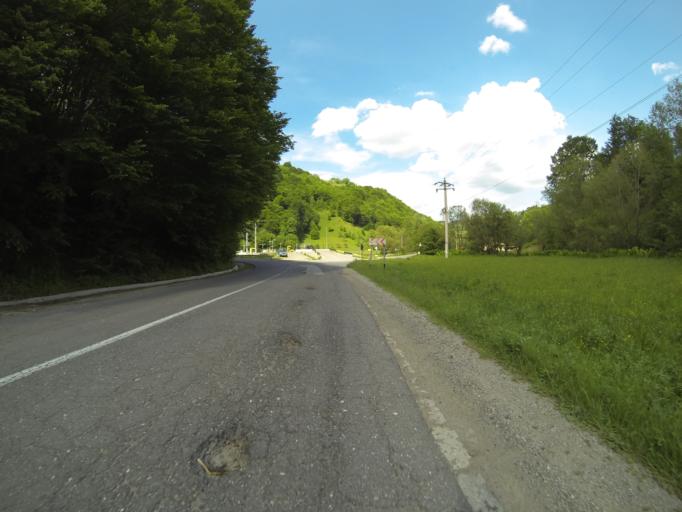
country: RO
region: Brasov
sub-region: Comuna Sinca Noua
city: Sinca Noua
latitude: 45.6544
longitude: 25.2826
